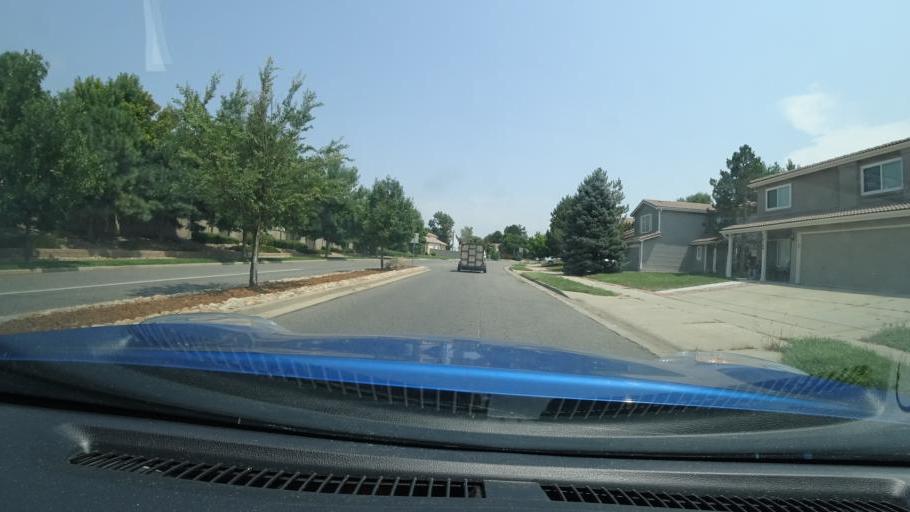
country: US
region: Colorado
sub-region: Adams County
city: Aurora
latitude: 39.7748
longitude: -104.7531
